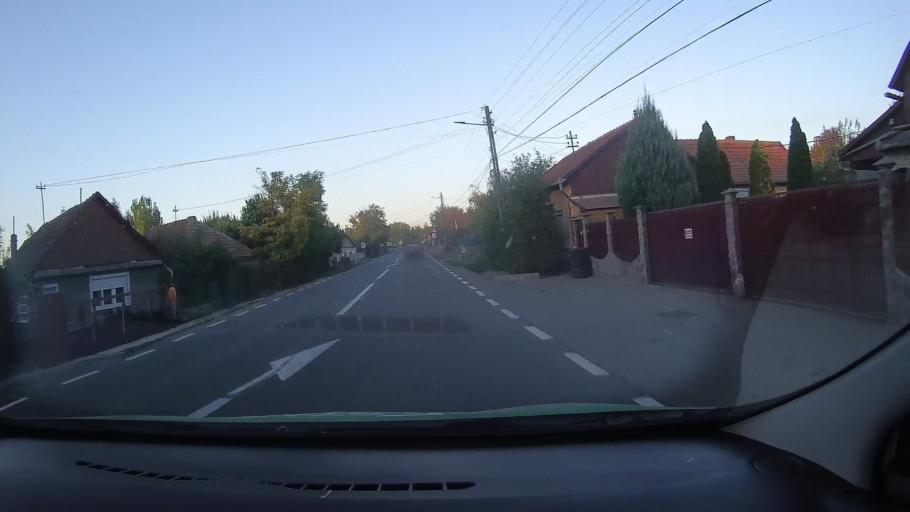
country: RO
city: Szekelyhid
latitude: 47.3346
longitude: 22.0872
